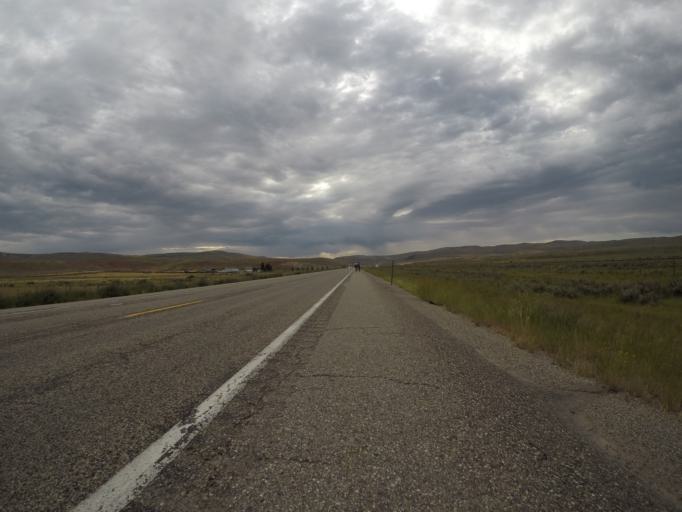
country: US
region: Utah
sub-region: Rich County
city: Randolph
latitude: 41.8251
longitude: -110.9137
